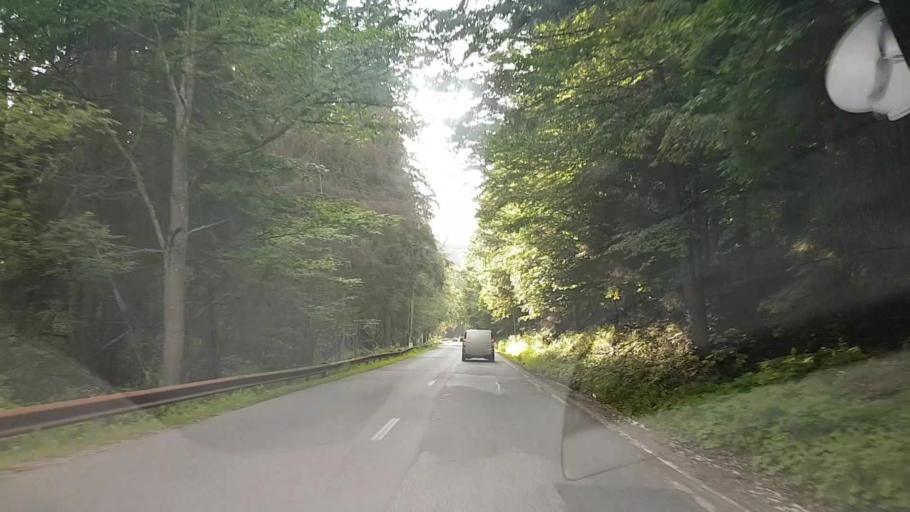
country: RO
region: Harghita
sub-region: Comuna Remetea
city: Remetea
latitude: 46.6734
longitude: 25.3429
